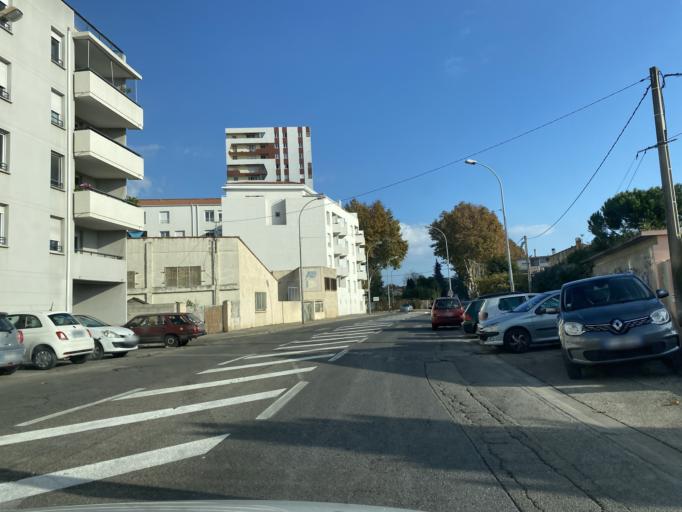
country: FR
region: Provence-Alpes-Cote d'Azur
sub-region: Departement du Var
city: La Seyne-sur-Mer
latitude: 43.1096
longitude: 5.8732
